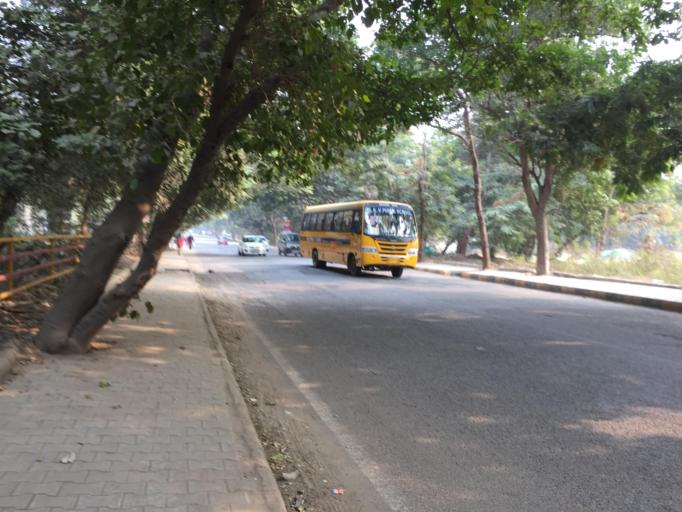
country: IN
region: Haryana
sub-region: Gurgaon
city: Gurgaon
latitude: 28.4247
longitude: 77.0964
